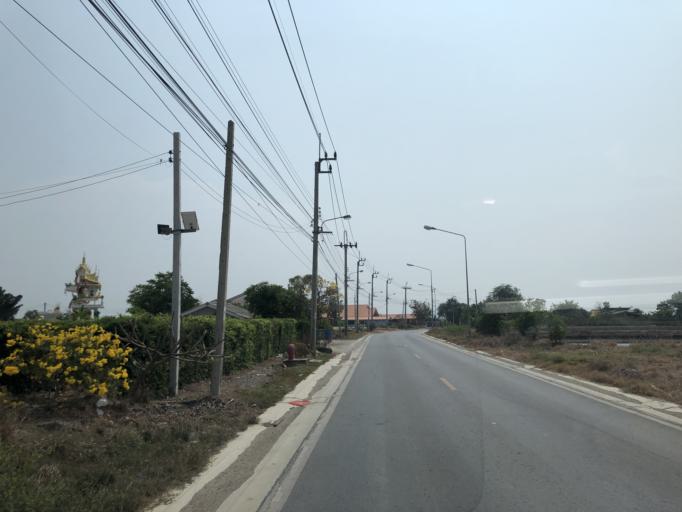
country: TH
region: Samut Prakan
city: Bang Bo
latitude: 13.5451
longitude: 100.8754
